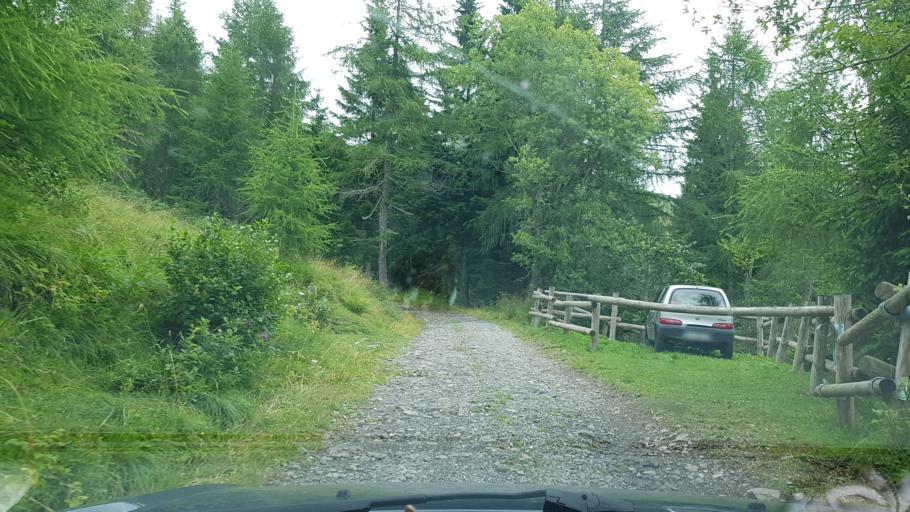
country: IT
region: Friuli Venezia Giulia
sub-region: Provincia di Udine
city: Cercivento
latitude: 46.5474
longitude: 12.9751
